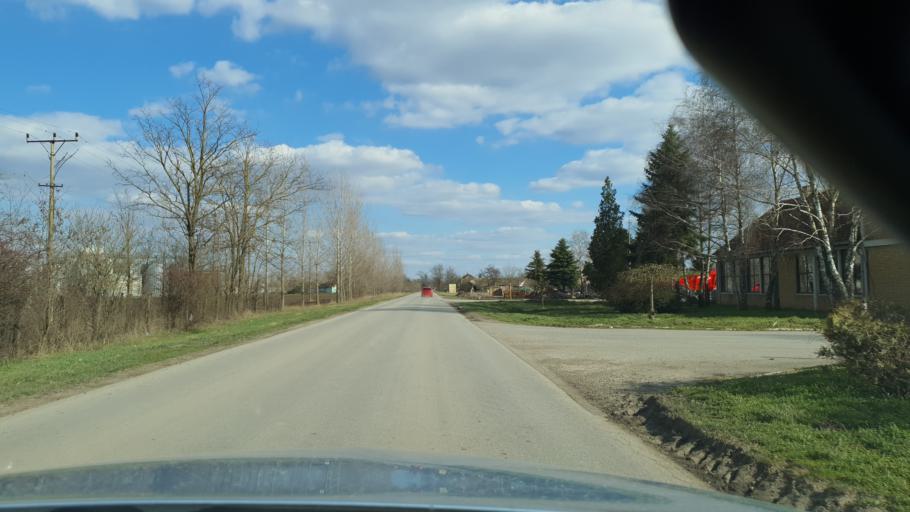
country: RS
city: Zmajevo
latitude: 45.4587
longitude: 19.6667
